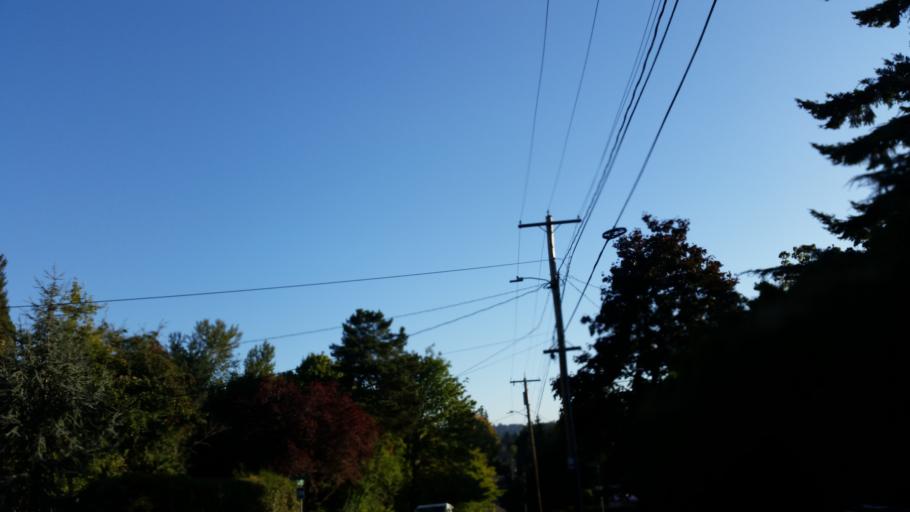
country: US
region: Oregon
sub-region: Washington County
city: Garden Home-Whitford
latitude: 45.4751
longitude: -122.7129
